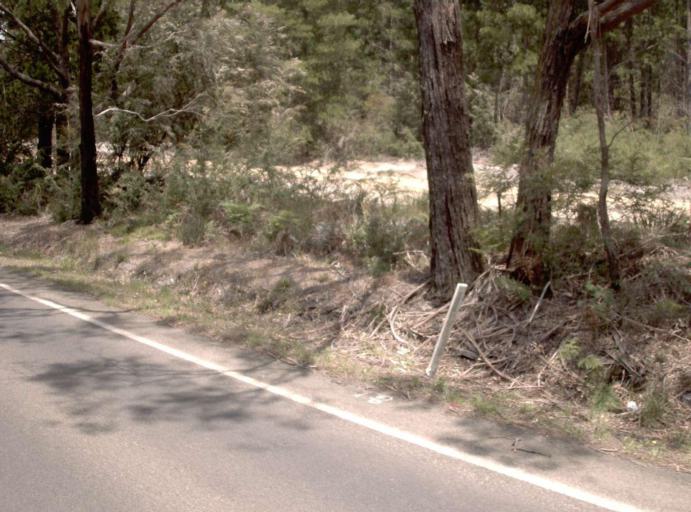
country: AU
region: Victoria
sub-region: Latrobe
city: Traralgon
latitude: -38.2688
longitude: 146.6917
